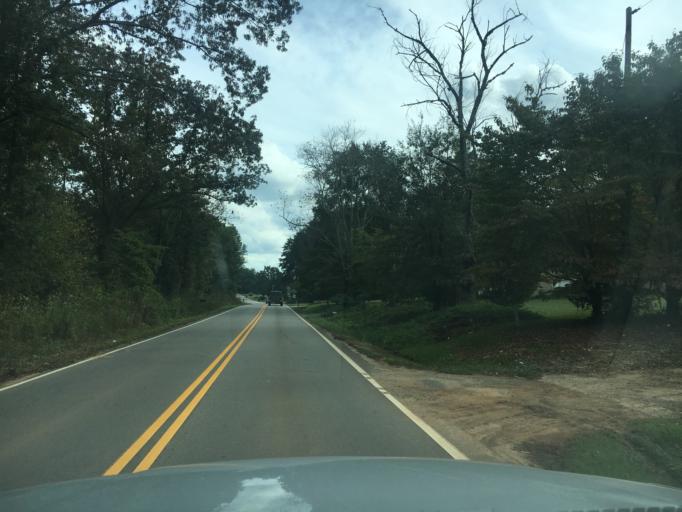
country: US
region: South Carolina
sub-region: Spartanburg County
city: Wellford
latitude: 34.9183
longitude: -82.0608
